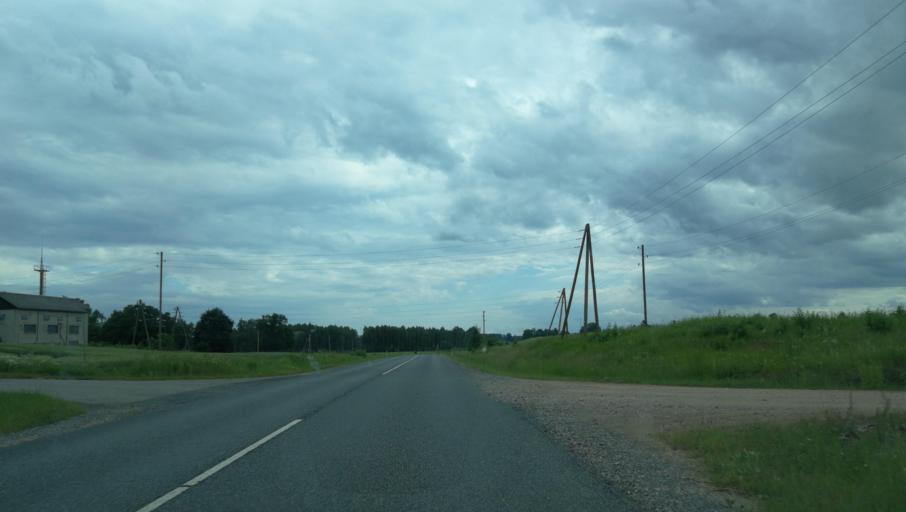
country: LV
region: Naukseni
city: Naukseni
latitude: 57.7477
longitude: 25.4323
